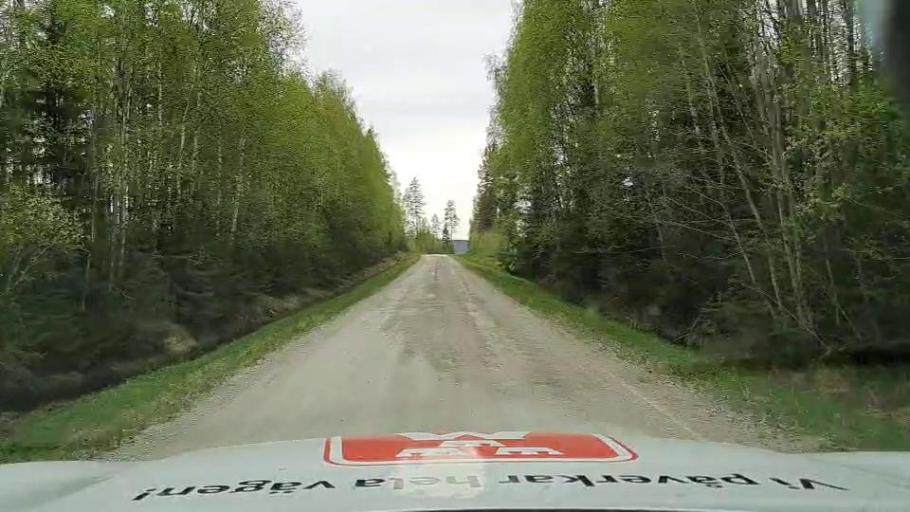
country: SE
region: Jaemtland
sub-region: Bergs Kommun
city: Hoverberg
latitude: 62.6775
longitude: 14.7600
